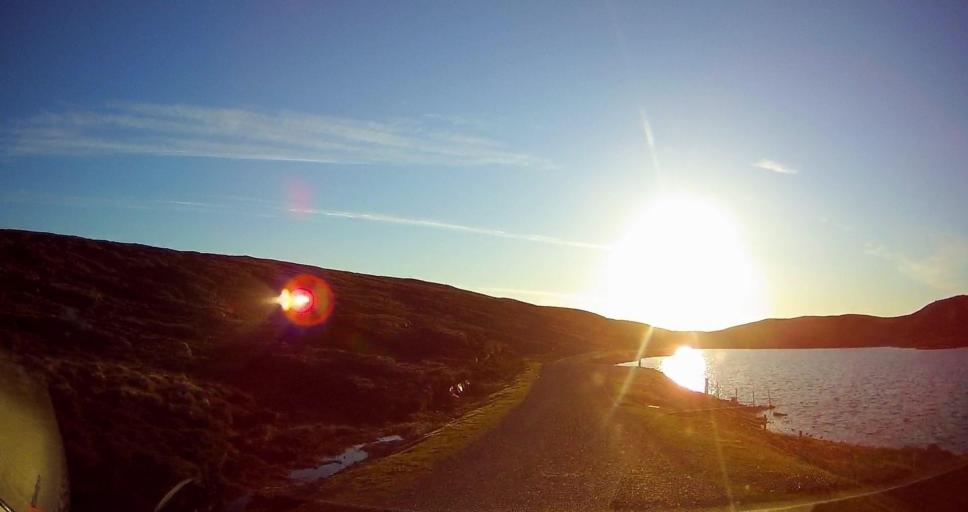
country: GB
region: Scotland
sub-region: Shetland Islands
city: Lerwick
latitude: 60.4428
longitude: -1.4048
